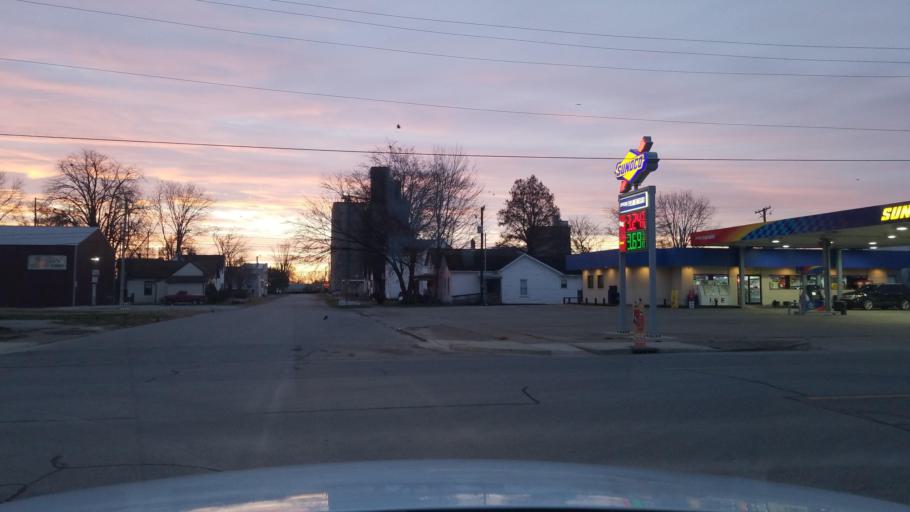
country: US
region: Indiana
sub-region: Posey County
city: Mount Vernon
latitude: 37.9307
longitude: -87.9020
